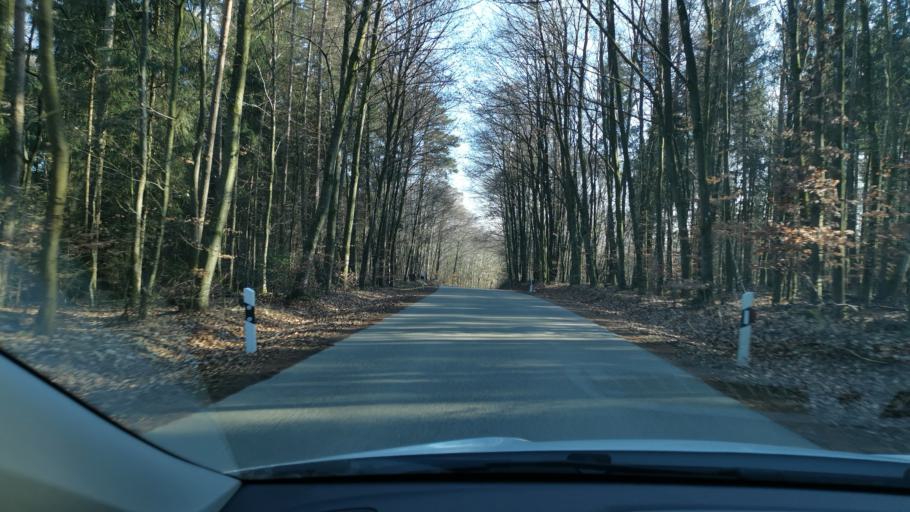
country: DE
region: Bavaria
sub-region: Swabia
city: Aindling
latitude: 48.5423
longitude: 10.9655
